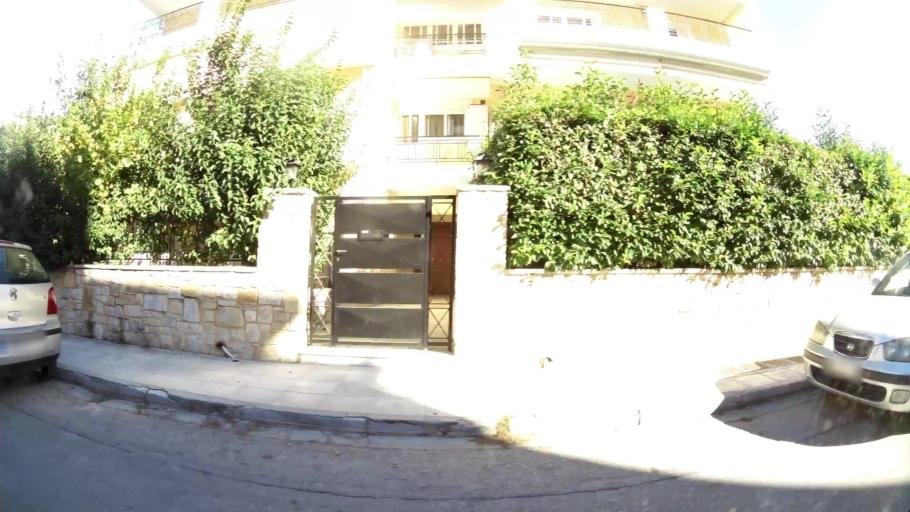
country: GR
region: Attica
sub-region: Nomarchia Anatolikis Attikis
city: Leondarion
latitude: 37.9854
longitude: 23.8495
